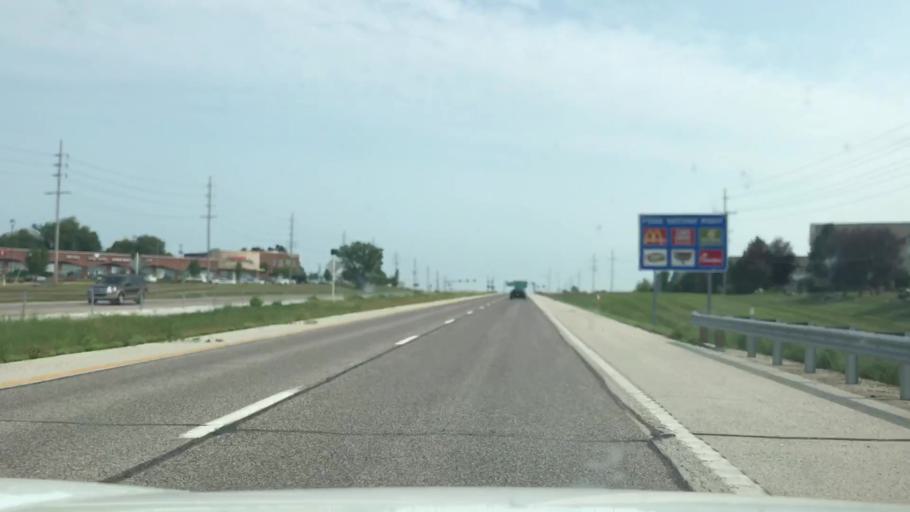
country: US
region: Missouri
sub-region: Saint Charles County
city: Cottleville
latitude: 38.7285
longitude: -90.6432
